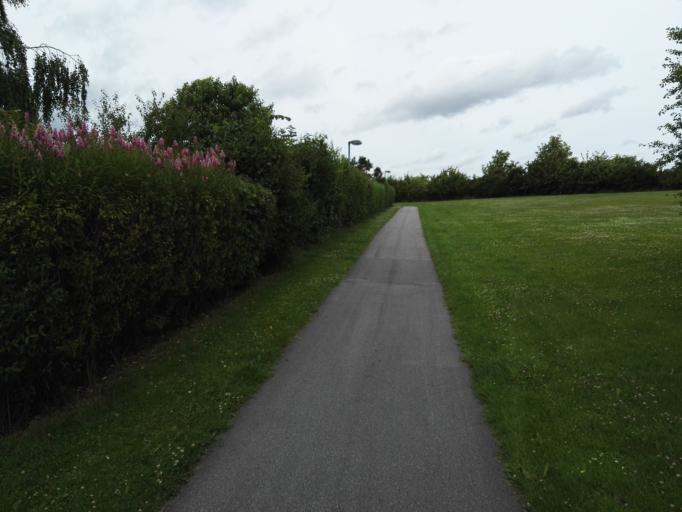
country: DK
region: Capital Region
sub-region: Egedal Kommune
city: Stenlose
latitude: 55.7706
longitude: 12.1811
